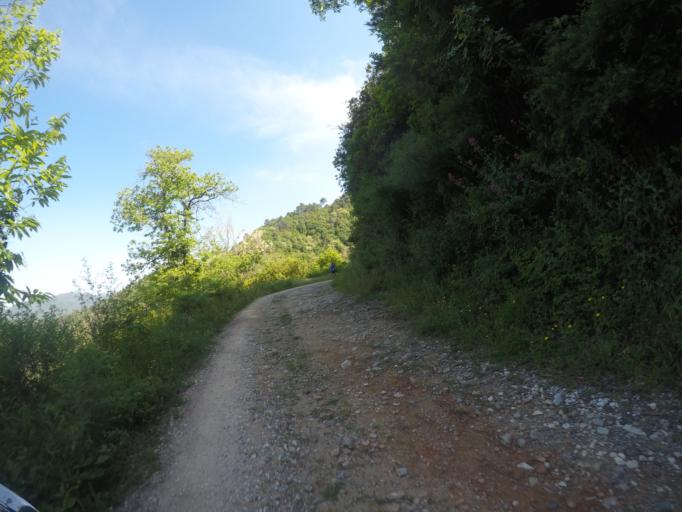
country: IT
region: Tuscany
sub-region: Provincia di Massa-Carrara
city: Massa
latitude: 44.0528
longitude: 10.1019
